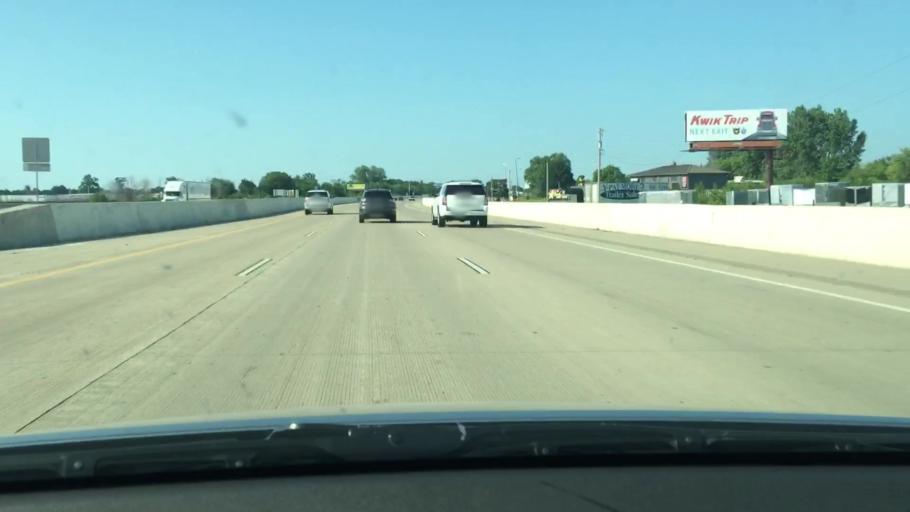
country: US
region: Wisconsin
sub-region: Winnebago County
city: Neenah
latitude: 44.1296
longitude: -88.4974
